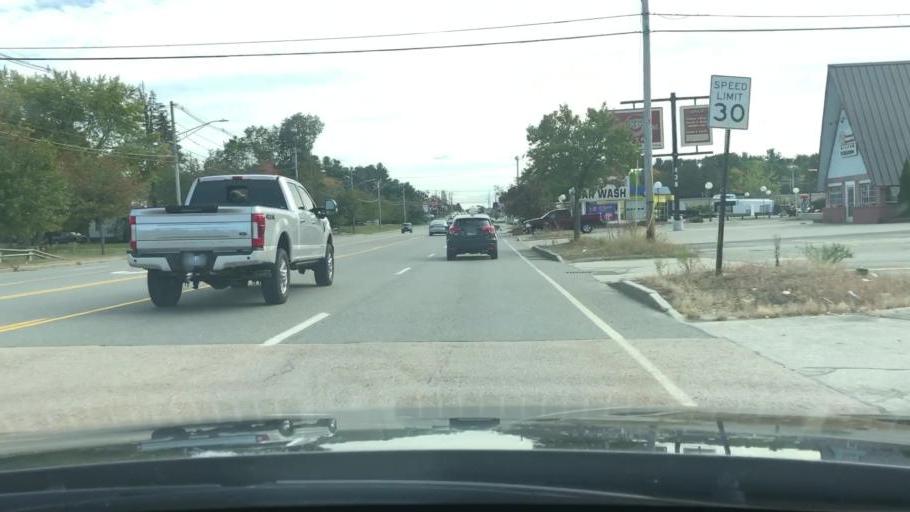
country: US
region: Massachusetts
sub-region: Essex County
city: Methuen
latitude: 42.7480
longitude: -71.2034
